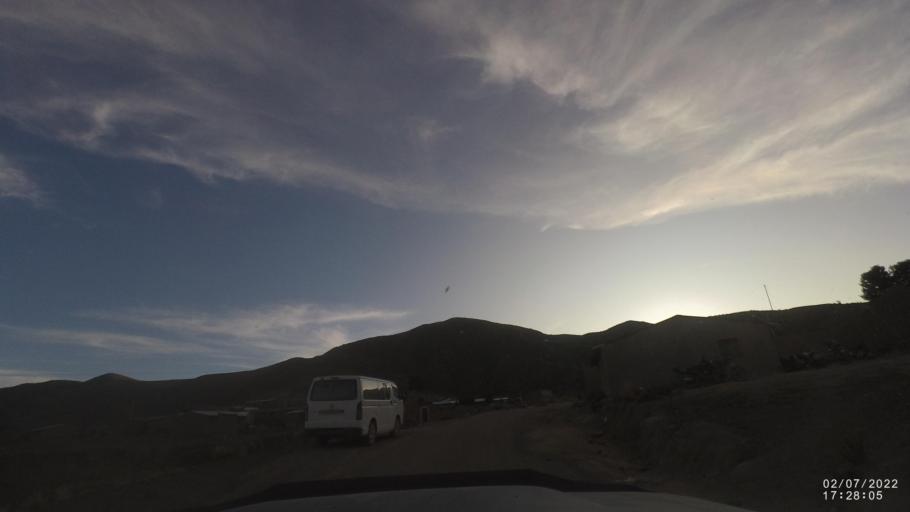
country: BO
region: Cochabamba
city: Irpa Irpa
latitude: -17.8830
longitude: -66.6163
